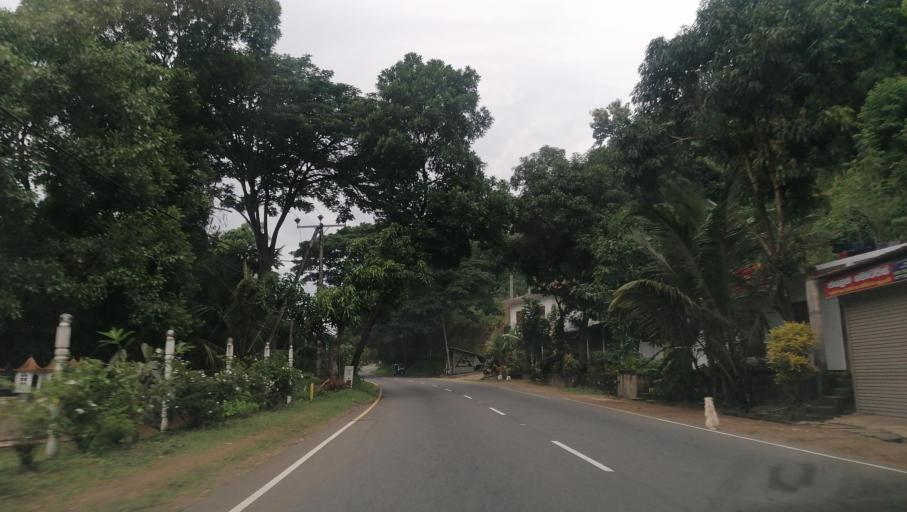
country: LK
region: Central
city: Kandy
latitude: 7.2458
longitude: 80.7245
